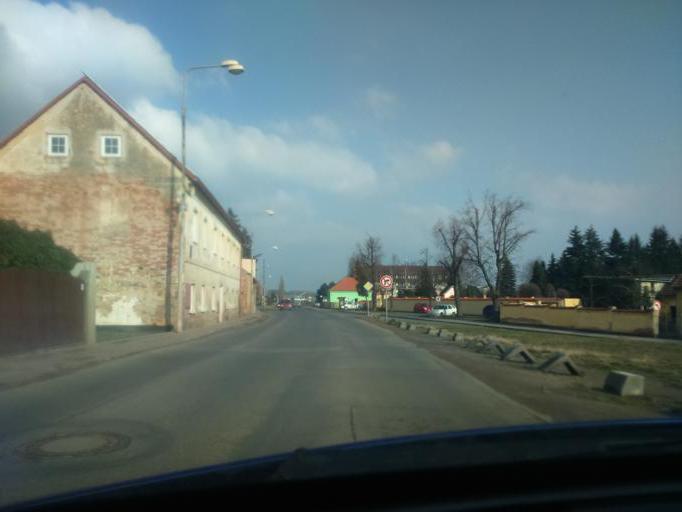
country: CZ
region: Plzensky
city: Chotesov
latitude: 49.6555
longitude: 13.2045
